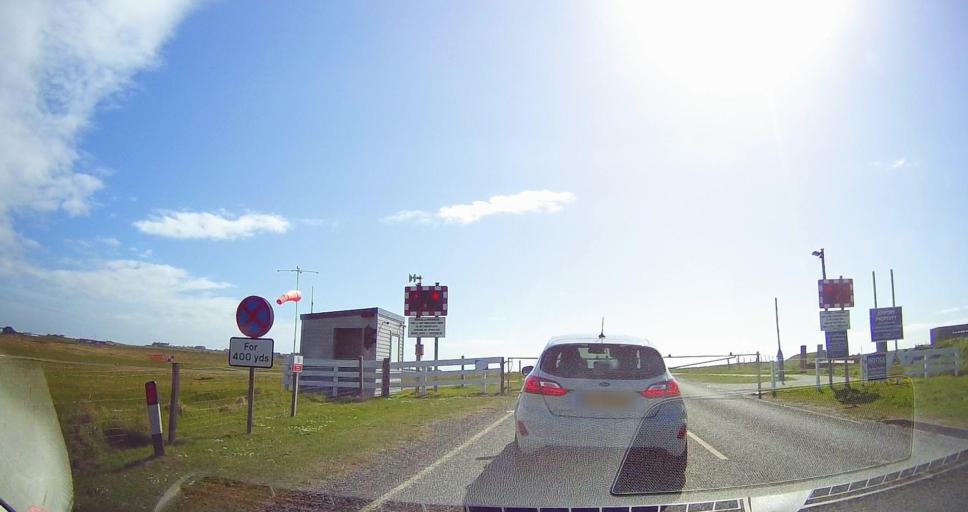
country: GB
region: Scotland
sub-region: Shetland Islands
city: Sandwick
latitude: 59.8824
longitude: -1.3032
